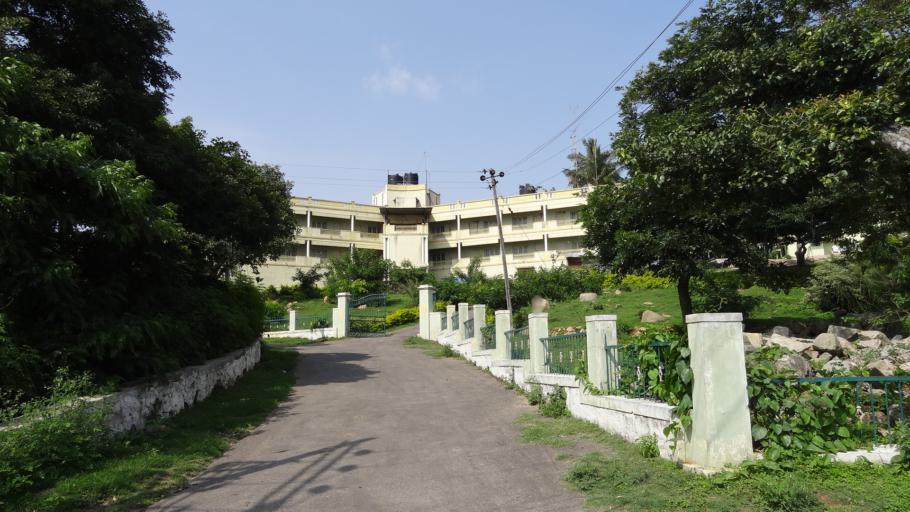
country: IN
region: Karnataka
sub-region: Mysore
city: Mysore
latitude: 12.2745
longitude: 76.6697
